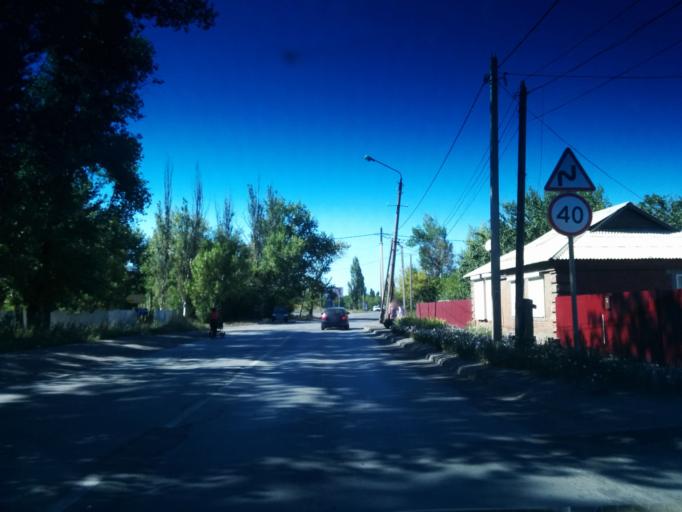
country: RU
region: Rostov
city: Shakhty
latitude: 47.6822
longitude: 40.2774
